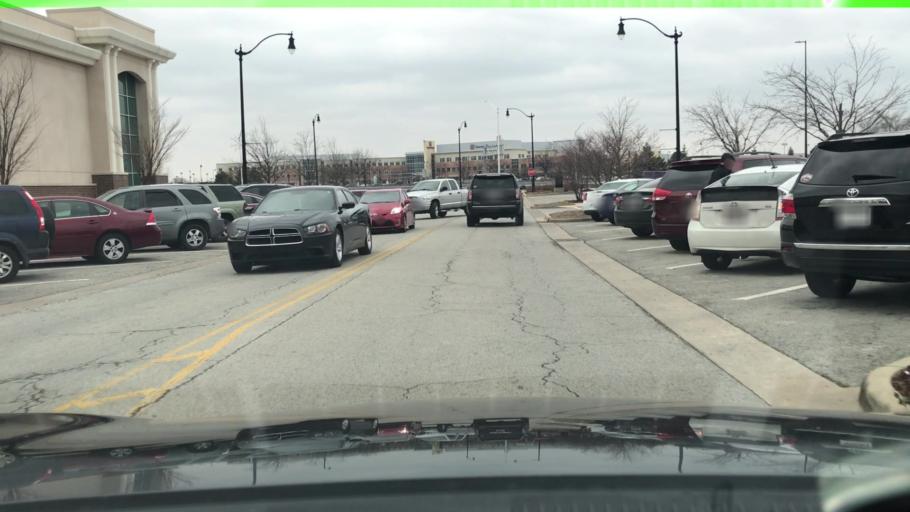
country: US
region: Indiana
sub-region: Hancock County
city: McCordsville
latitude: 39.9910
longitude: -85.9301
